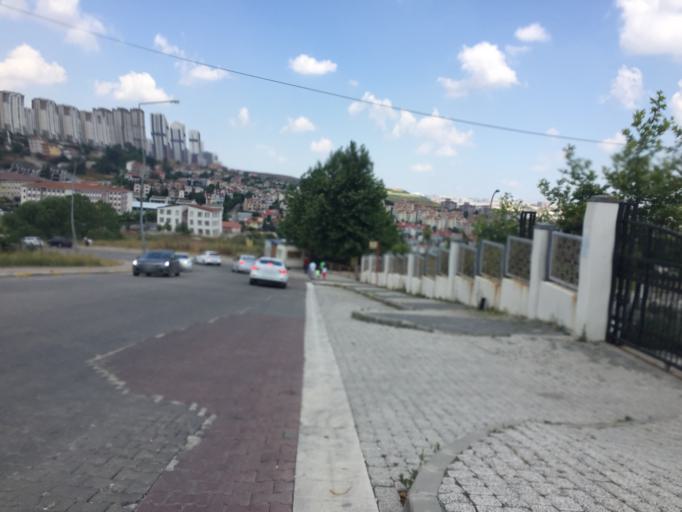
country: TR
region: Istanbul
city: Esenyurt
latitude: 41.0783
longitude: 28.6657
